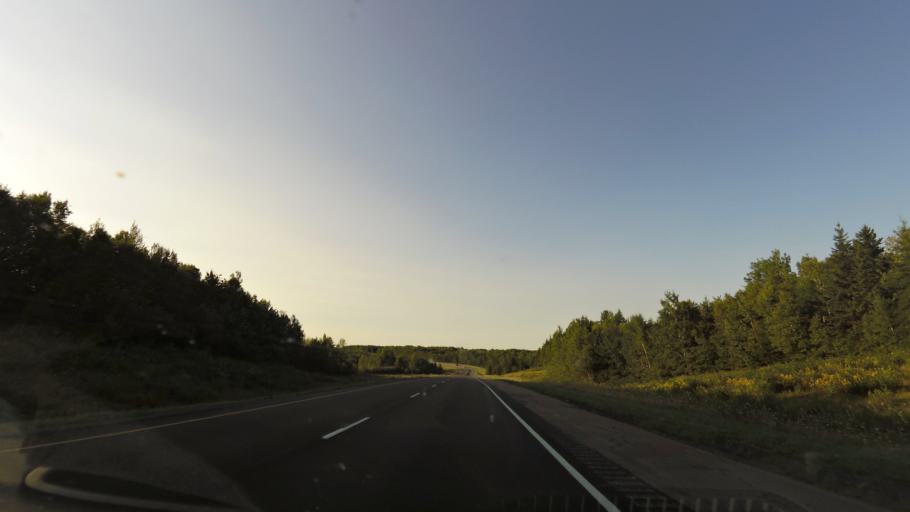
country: CA
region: New Brunswick
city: Dieppe
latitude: 46.0881
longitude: -64.5955
